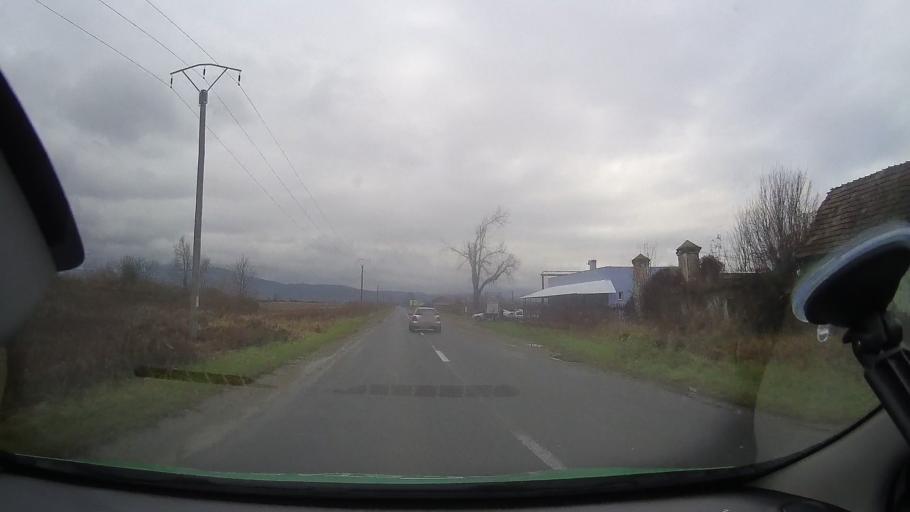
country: RO
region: Arad
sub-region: Comuna Sebis
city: Sebis
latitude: 46.3421
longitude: 22.1283
